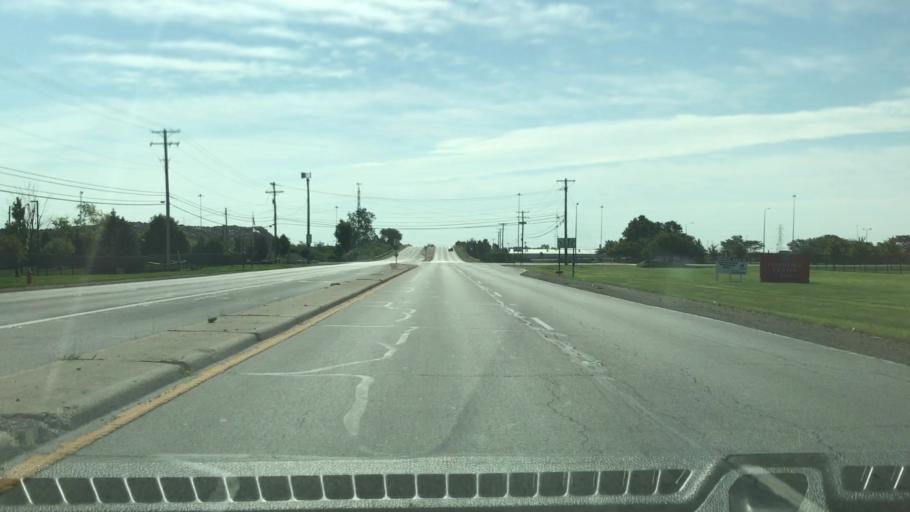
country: US
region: Ohio
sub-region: Franklin County
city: Lincoln Village
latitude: 39.9716
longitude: -83.1246
